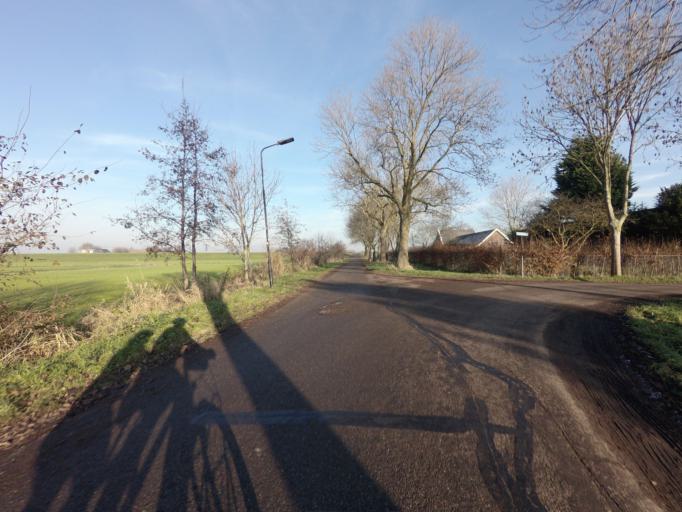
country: NL
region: Utrecht
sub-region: Gemeente De Ronde Venen
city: Mijdrecht
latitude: 52.2108
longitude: 4.8432
